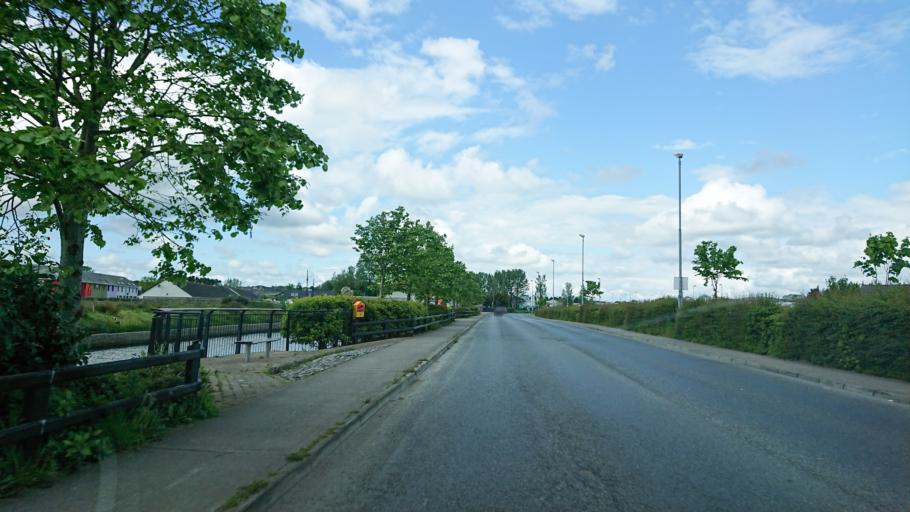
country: IE
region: Munster
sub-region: Waterford
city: Dungarvan
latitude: 52.0920
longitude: -7.6267
